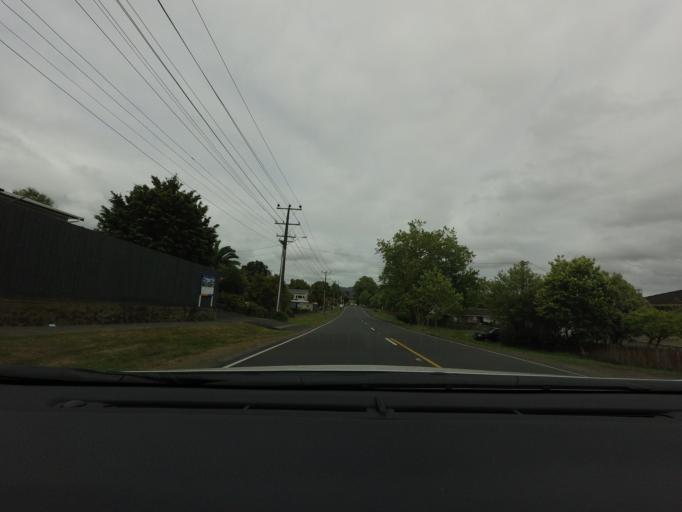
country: NZ
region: Auckland
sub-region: Auckland
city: Waitakere
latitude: -36.8941
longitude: 174.6189
